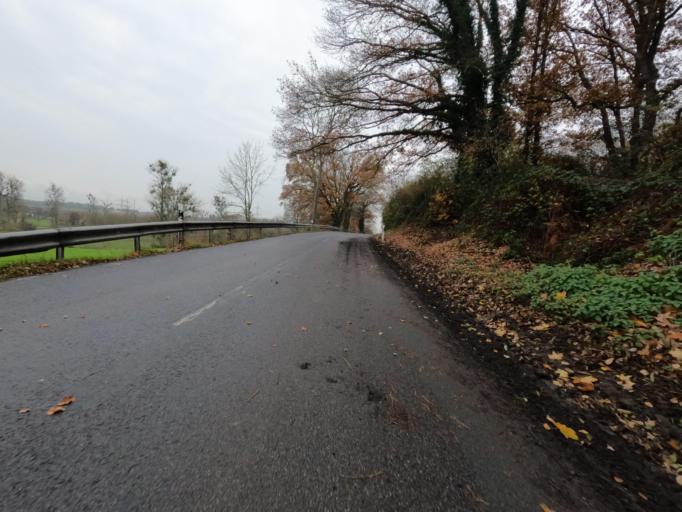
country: DE
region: North Rhine-Westphalia
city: Geilenkirchen
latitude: 50.9791
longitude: 6.1419
